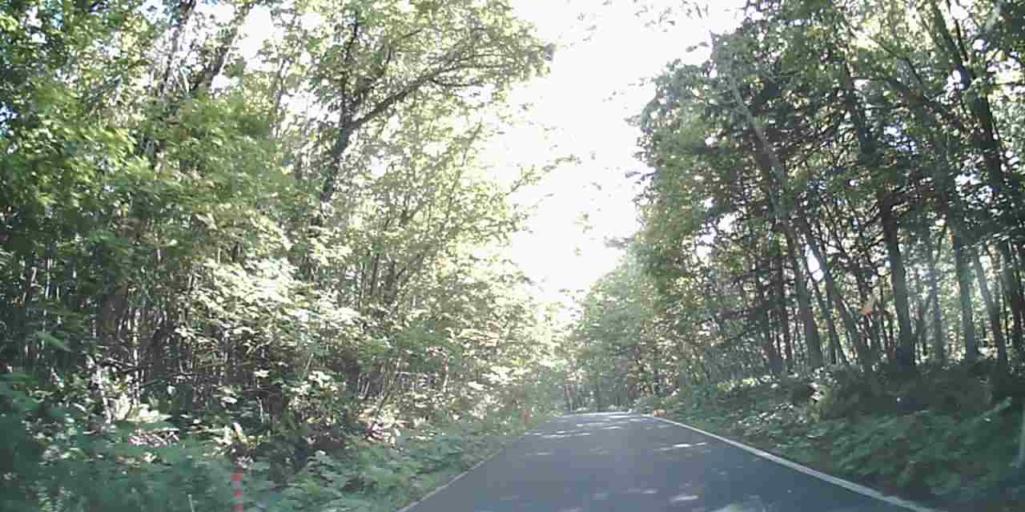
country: JP
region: Hokkaido
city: Shiraoi
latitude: 42.7208
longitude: 141.4119
